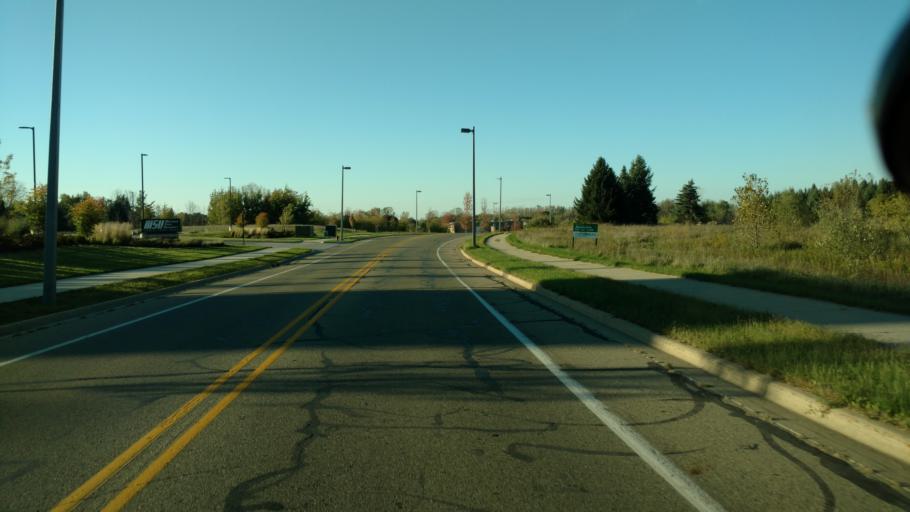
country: US
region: Michigan
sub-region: Ingham County
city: East Lansing
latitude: 42.7816
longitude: -84.5079
